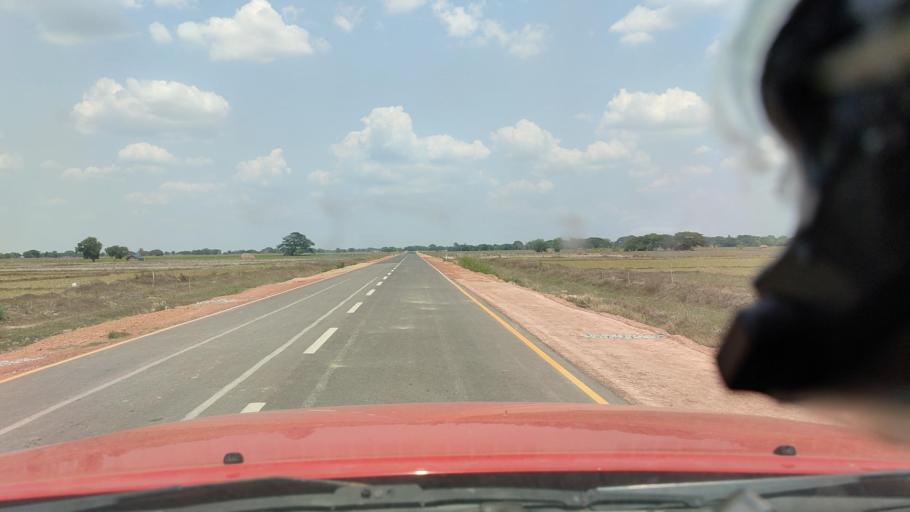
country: MM
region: Bago
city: Thanatpin
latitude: 17.0409
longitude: 96.3535
